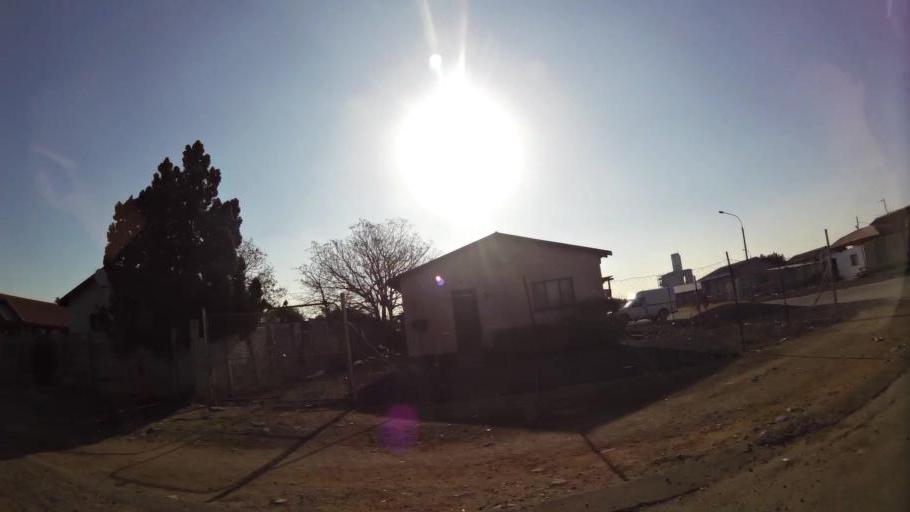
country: ZA
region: North-West
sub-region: Bojanala Platinum District Municipality
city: Rustenburg
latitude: -25.6414
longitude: 27.2375
